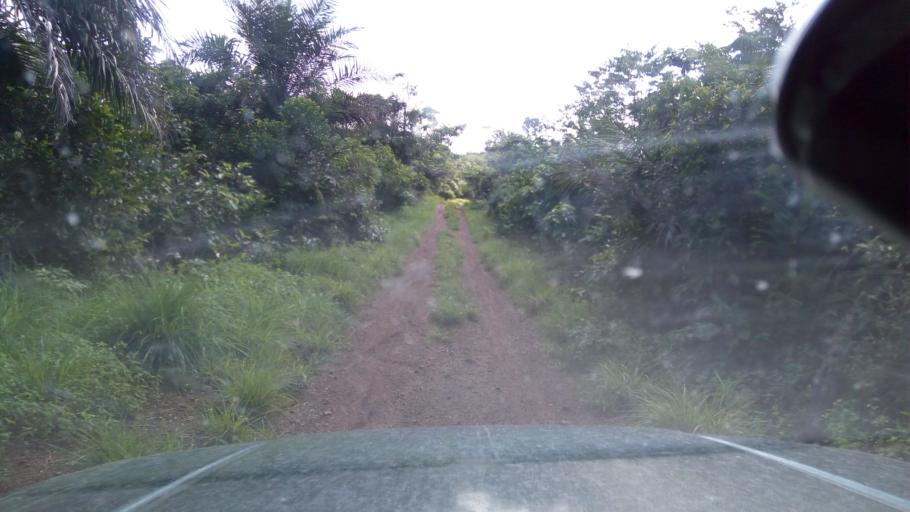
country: SL
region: Southern Province
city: Koribundu
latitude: 7.7324
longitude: -11.5092
